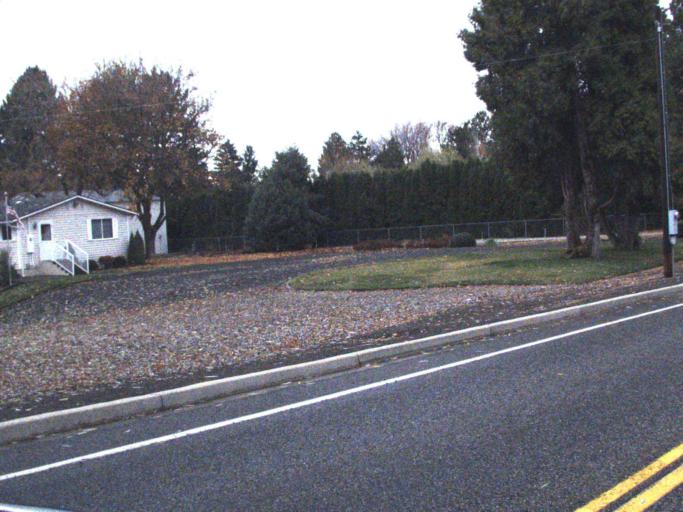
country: US
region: Washington
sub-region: Walla Walla County
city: Waitsburg
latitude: 46.2625
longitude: -118.1532
